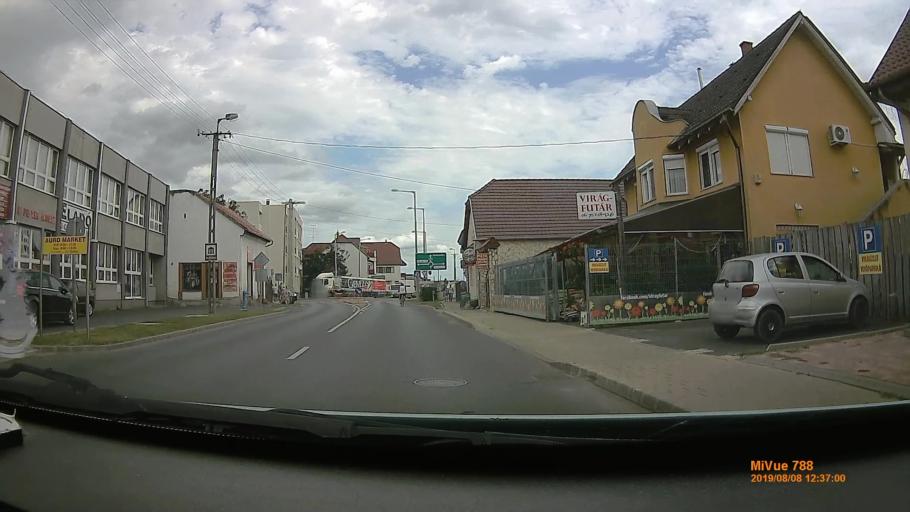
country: HU
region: Szabolcs-Szatmar-Bereg
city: Nyirbator
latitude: 47.8361
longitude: 22.1344
